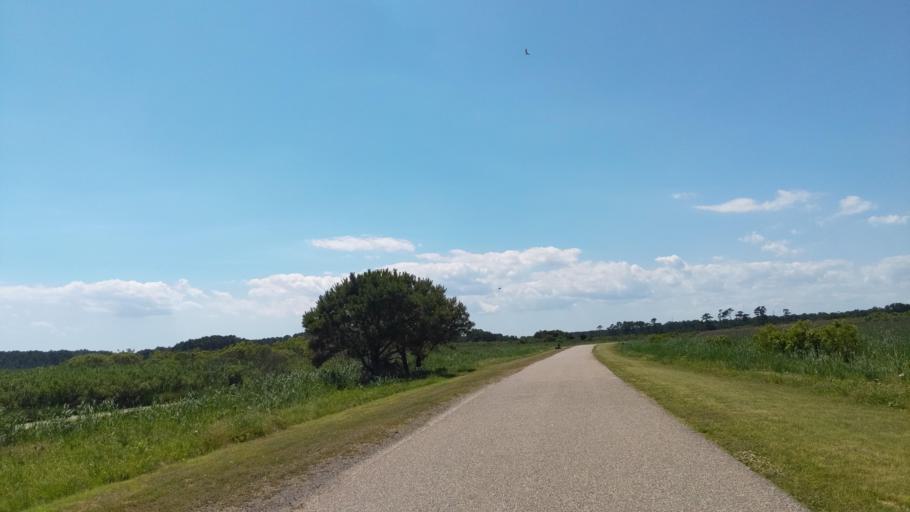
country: US
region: Virginia
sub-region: Accomack County
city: Chincoteague
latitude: 37.9015
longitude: -75.3468
